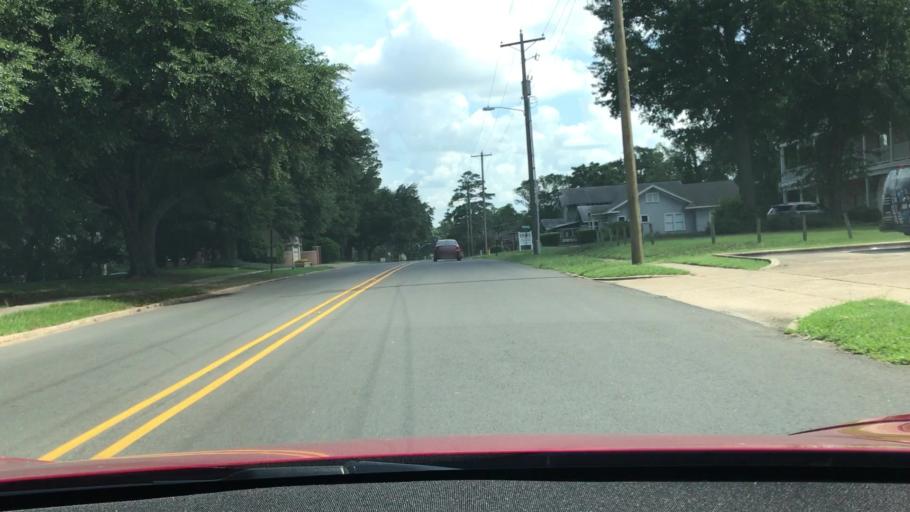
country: US
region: Louisiana
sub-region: Bossier Parish
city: Bossier City
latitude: 32.4845
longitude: -93.7339
